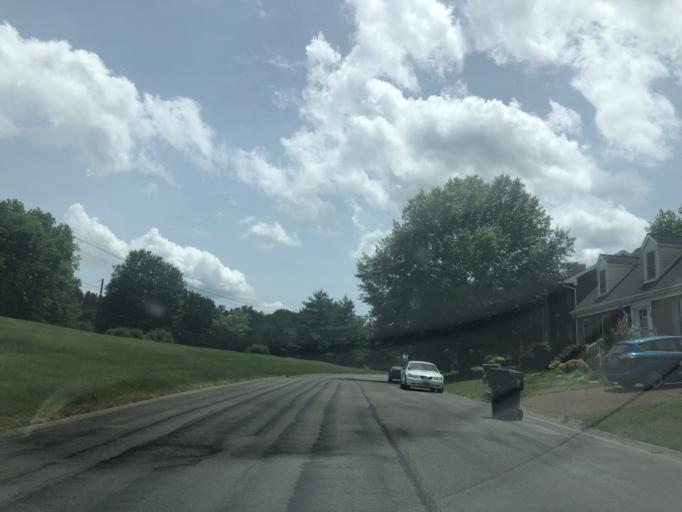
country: US
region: Tennessee
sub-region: Davidson County
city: Belle Meade
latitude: 36.0516
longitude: -86.9527
